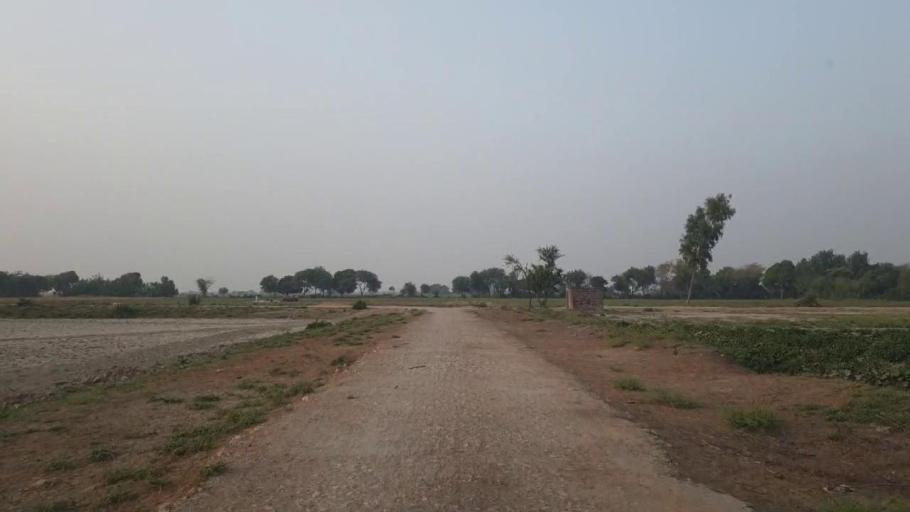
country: PK
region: Sindh
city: Mirpur Batoro
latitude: 24.6625
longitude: 68.3844
